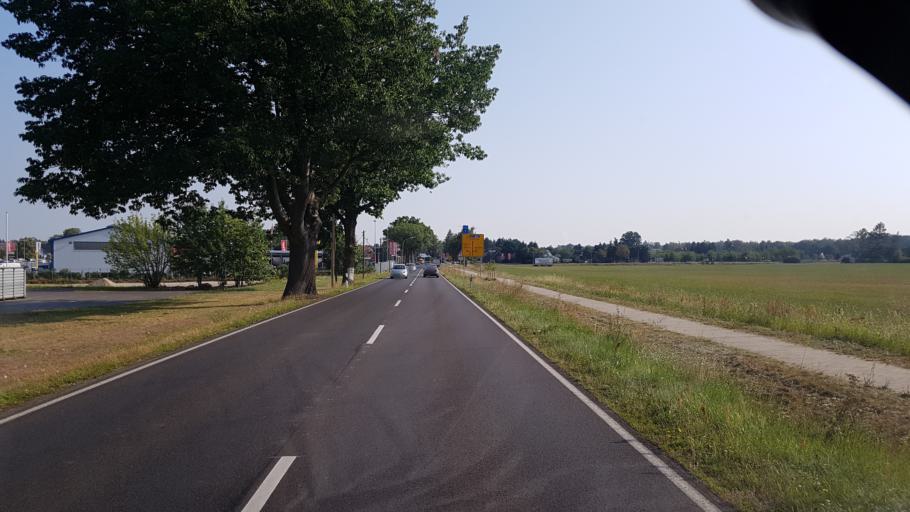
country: DE
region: Brandenburg
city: Kolkwitz
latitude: 51.7156
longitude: 14.2897
